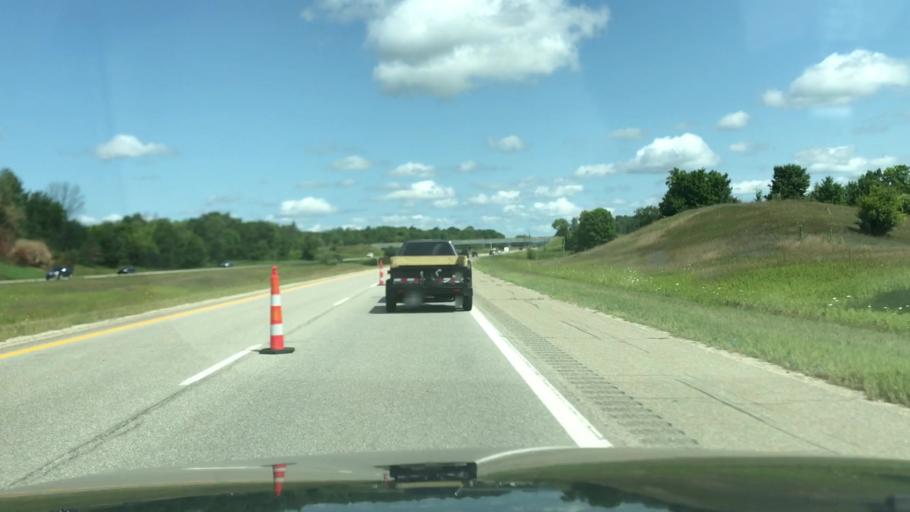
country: US
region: Michigan
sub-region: Mecosta County
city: Big Rapids
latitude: 43.7670
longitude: -85.5343
